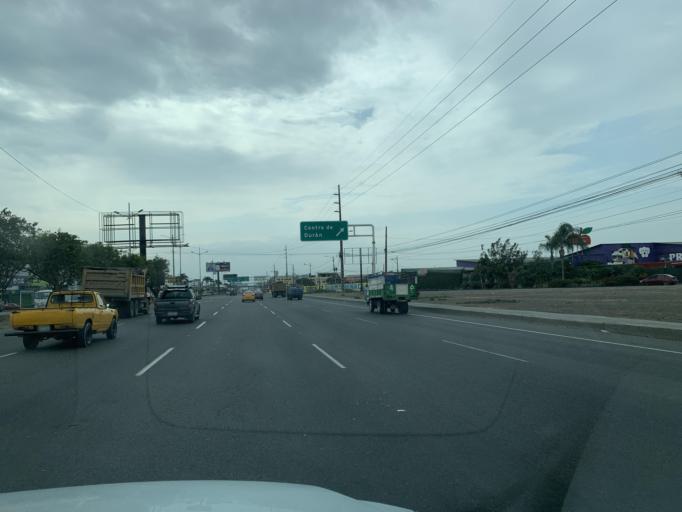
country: EC
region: Guayas
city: Eloy Alfaro
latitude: -2.1738
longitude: -79.8324
